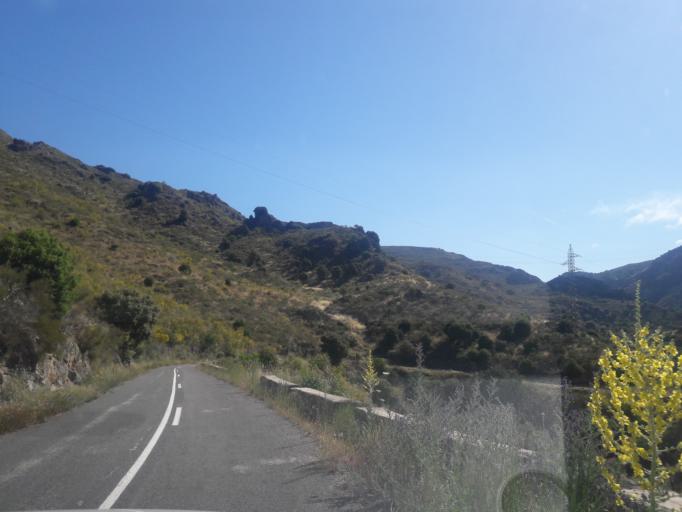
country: ES
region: Castille and Leon
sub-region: Provincia de Salamanca
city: Saucelle
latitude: 41.0286
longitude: -6.7398
